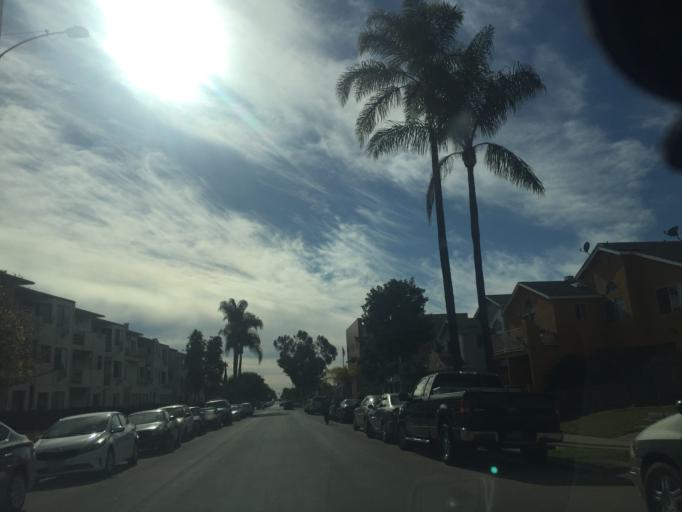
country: US
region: California
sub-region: San Diego County
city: Lemon Grove
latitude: 32.7544
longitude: -117.0965
